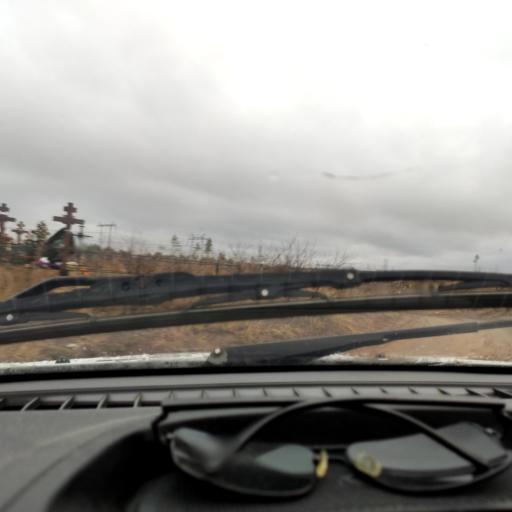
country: RU
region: Samara
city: Zhigulevsk
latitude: 53.5372
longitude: 49.5531
